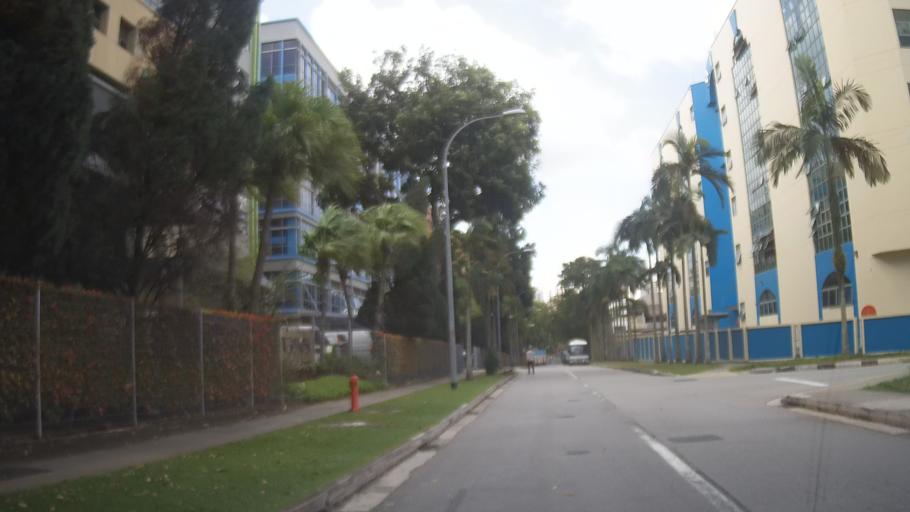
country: MY
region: Johor
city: Johor Bahru
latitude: 1.4062
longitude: 103.7593
